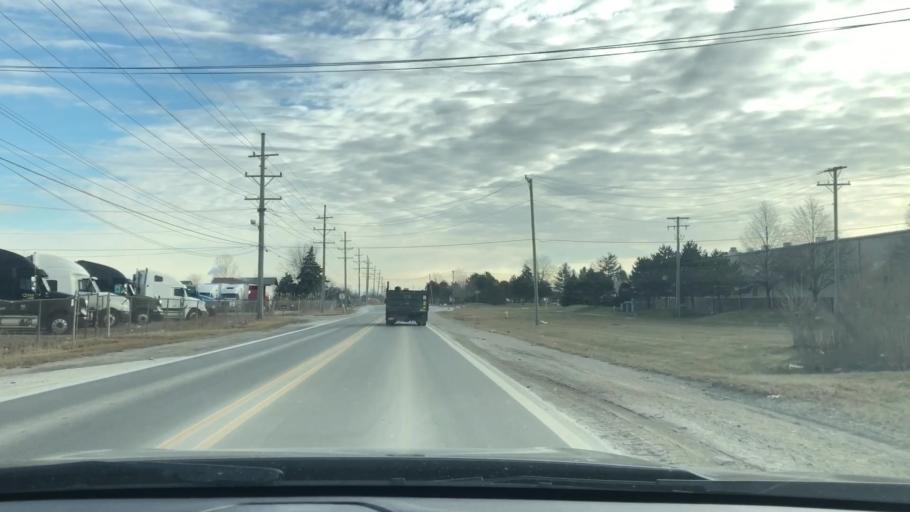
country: US
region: Michigan
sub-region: Macomb County
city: New Haven
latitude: 42.7191
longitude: -82.8076
